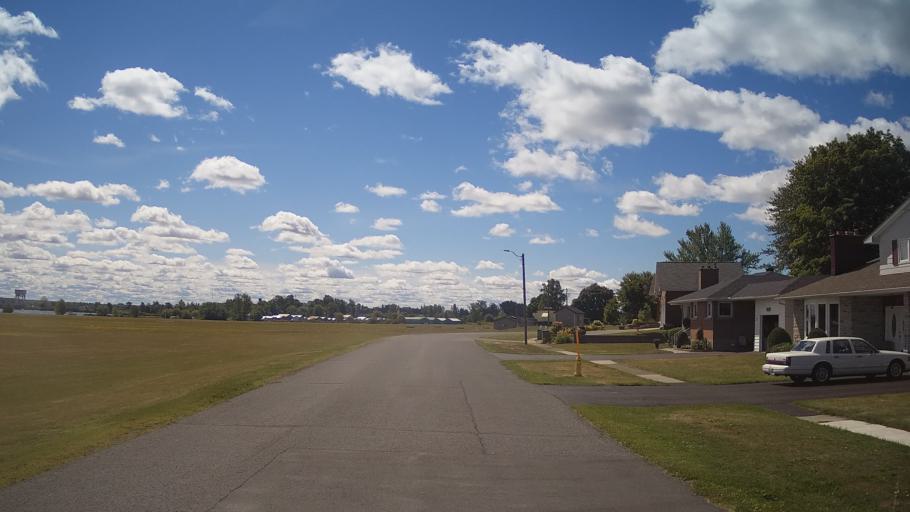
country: US
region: New York
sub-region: St. Lawrence County
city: Ogdensburg
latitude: 44.8453
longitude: -75.3123
